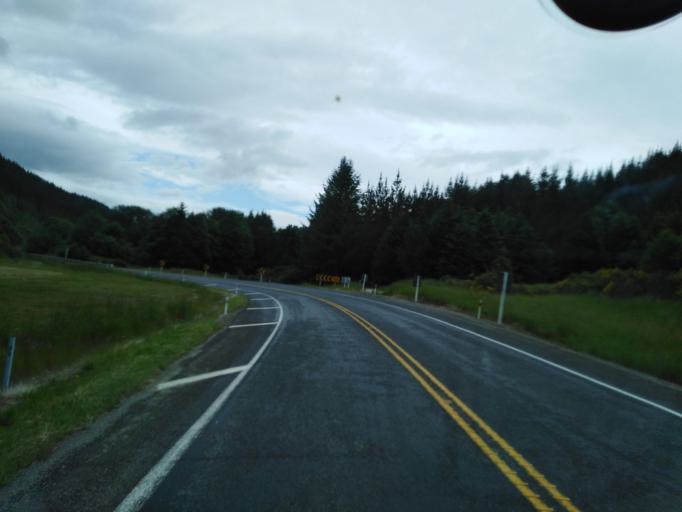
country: NZ
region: Tasman
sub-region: Tasman District
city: Wakefield
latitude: -41.4838
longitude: 172.8863
